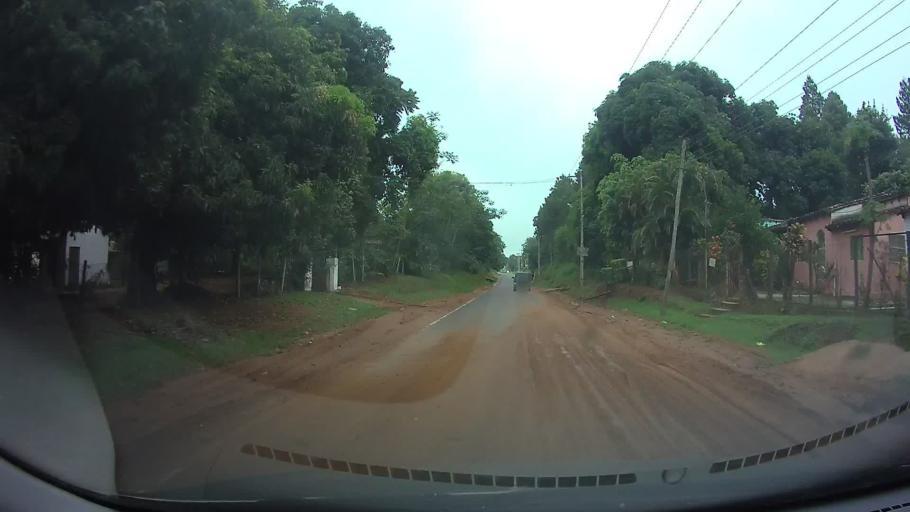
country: PY
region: Central
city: Itaugua
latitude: -25.3586
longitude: -57.3450
